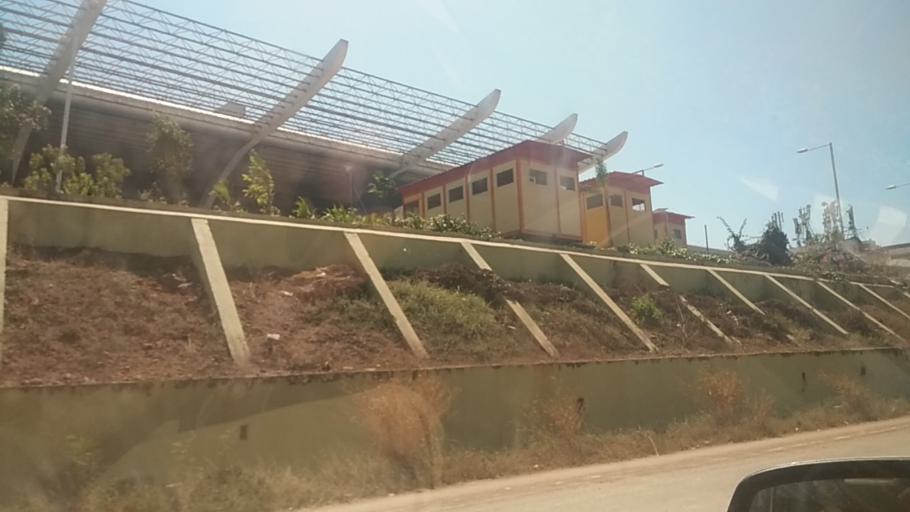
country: IN
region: Goa
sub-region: South Goa
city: Chicalim
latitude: 15.3857
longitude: 73.8367
